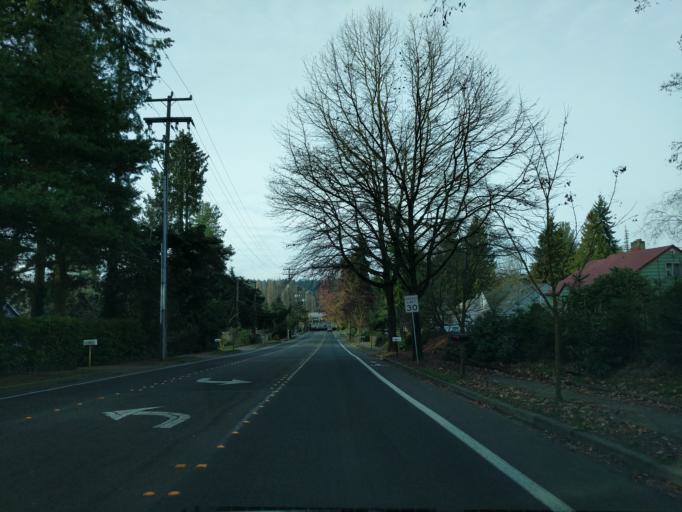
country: US
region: Washington
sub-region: King County
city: Shoreline
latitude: 47.7413
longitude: -122.3248
